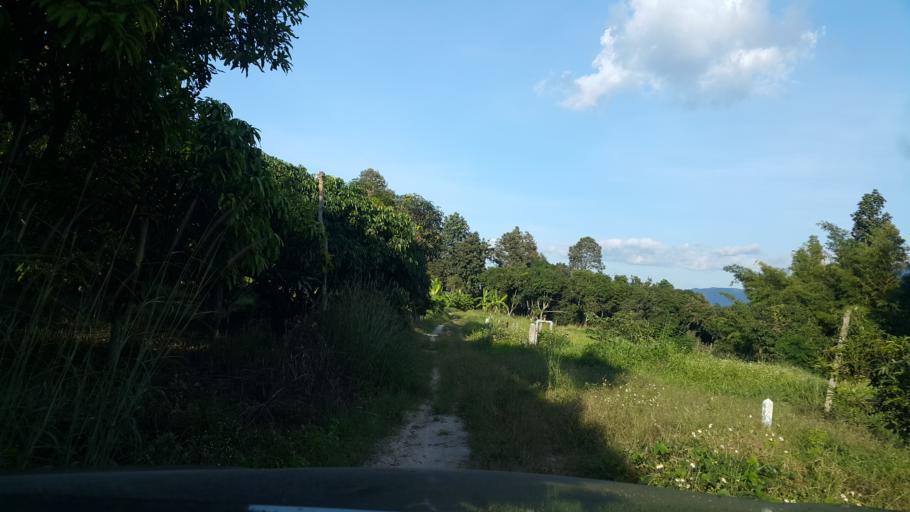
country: TH
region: Chiang Mai
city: Mae On
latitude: 18.7098
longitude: 99.1969
